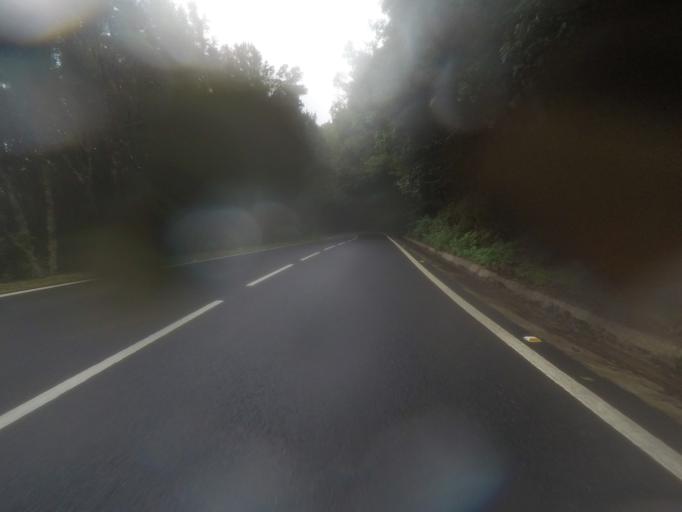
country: ES
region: Canary Islands
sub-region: Provincia de Santa Cruz de Tenerife
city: Vallehermosa
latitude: 28.1385
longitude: -17.2820
